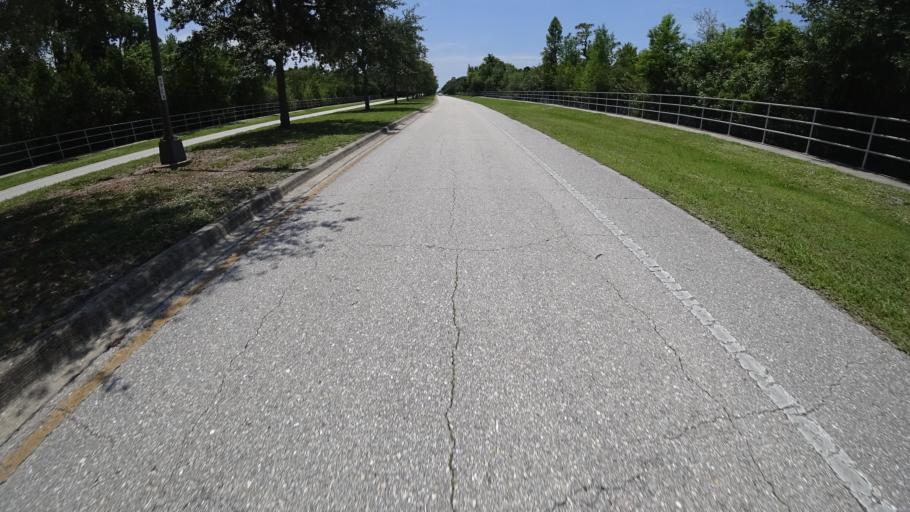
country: US
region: Florida
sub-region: Sarasota County
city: Desoto Lakes
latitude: 27.4037
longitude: -82.4632
